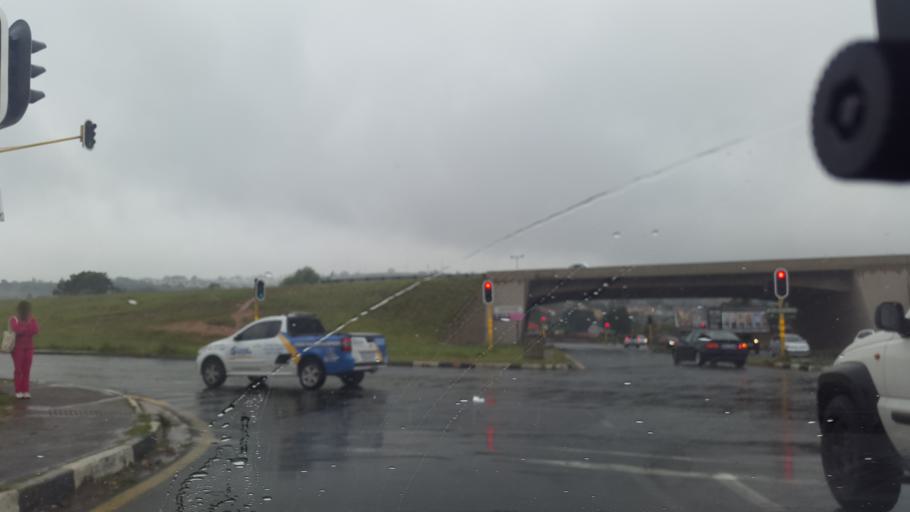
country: ZA
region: Gauteng
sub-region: City of Johannesburg Metropolitan Municipality
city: Johannesburg
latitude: -26.2709
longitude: 28.0314
